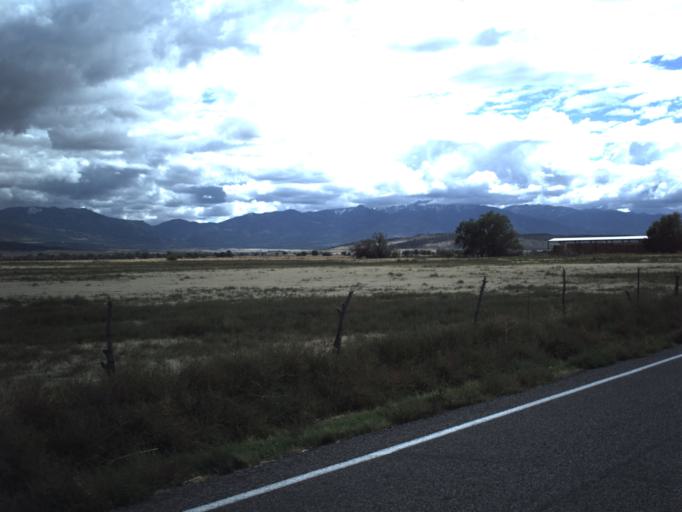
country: US
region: Utah
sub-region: Millard County
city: Fillmore
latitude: 39.0623
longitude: -112.4098
